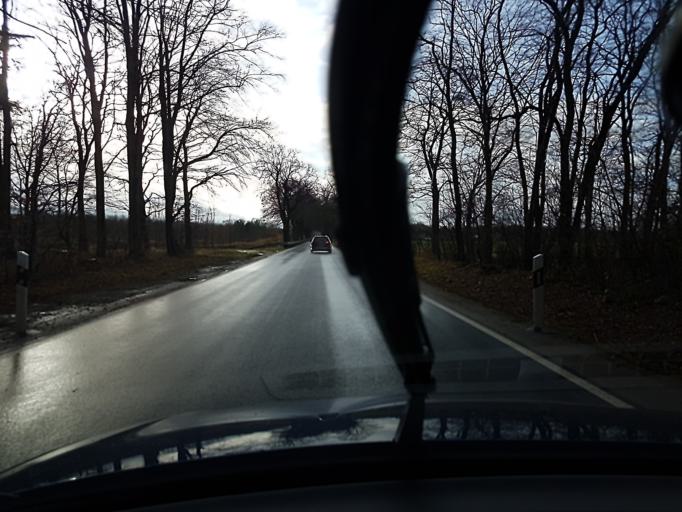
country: DE
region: Mecklenburg-Vorpommern
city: Bad Sulze
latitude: 54.0729
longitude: 12.6801
